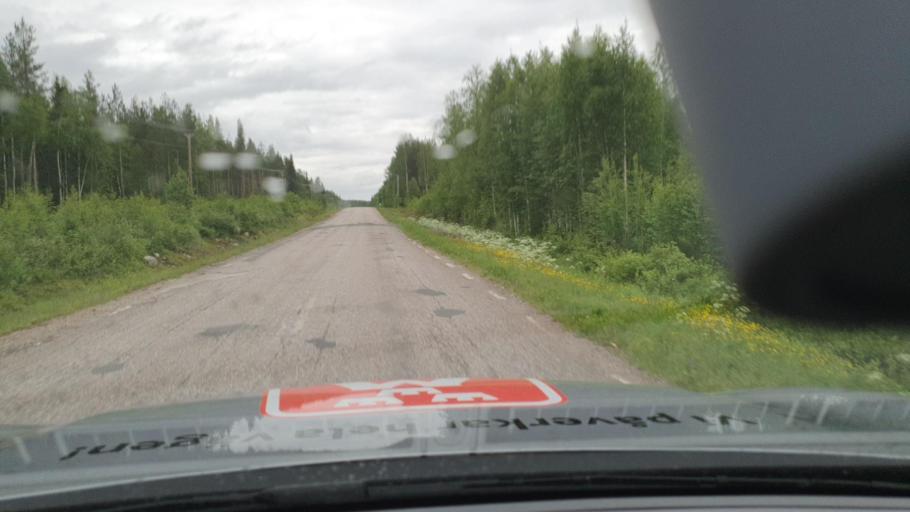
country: SE
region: Norrbotten
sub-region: Overkalix Kommun
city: OEverkalix
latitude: 66.3941
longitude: 22.7904
